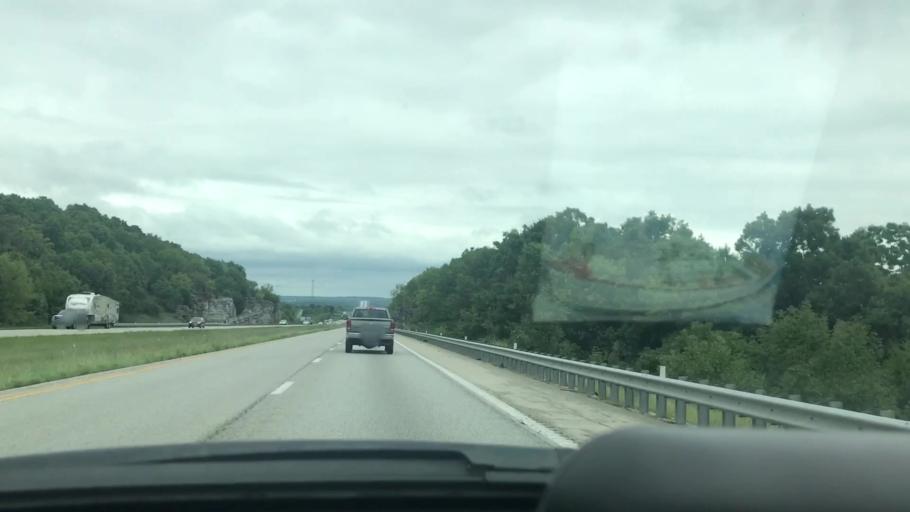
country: US
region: Missouri
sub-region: Lawrence County
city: Mount Vernon
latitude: 37.1473
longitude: -93.7075
